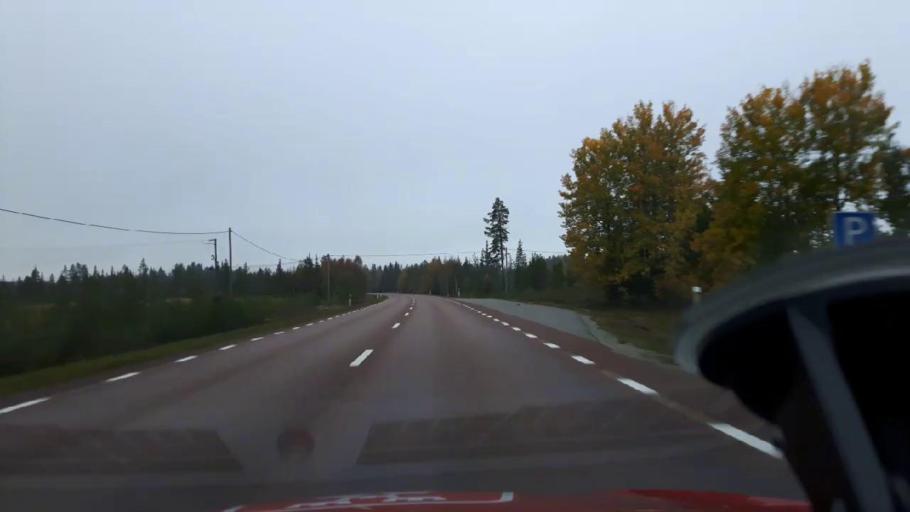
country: SE
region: Jaemtland
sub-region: Bergs Kommun
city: Hoverberg
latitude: 62.5117
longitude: 14.4497
